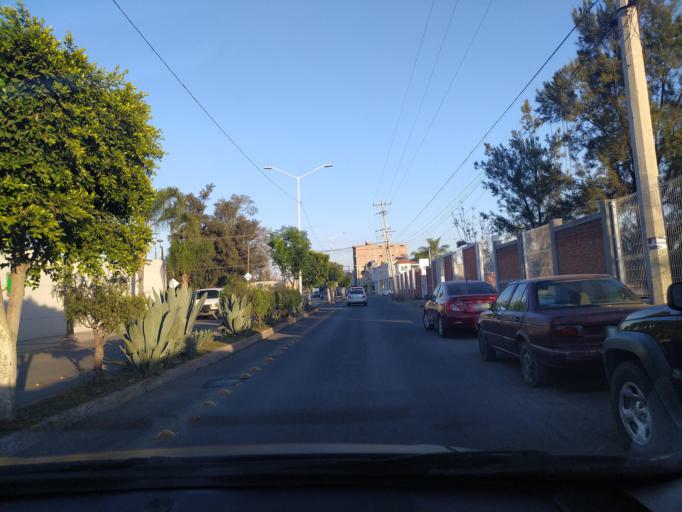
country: MX
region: Guanajuato
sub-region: San Francisco del Rincon
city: Fraccionamiento la Mezquitera
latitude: 21.0123
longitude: -101.8400
